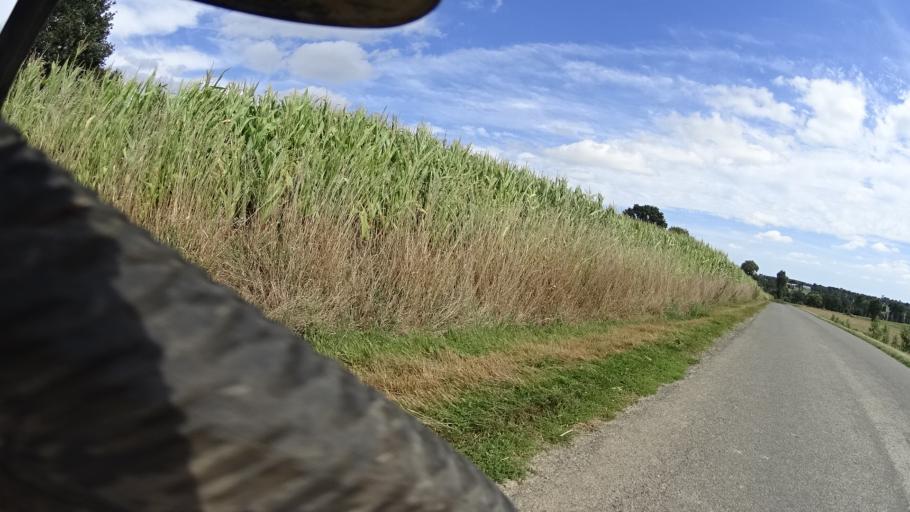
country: FR
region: Brittany
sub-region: Departement d'Ille-et-Vilaine
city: Vignoc
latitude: 48.2336
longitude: -1.7716
